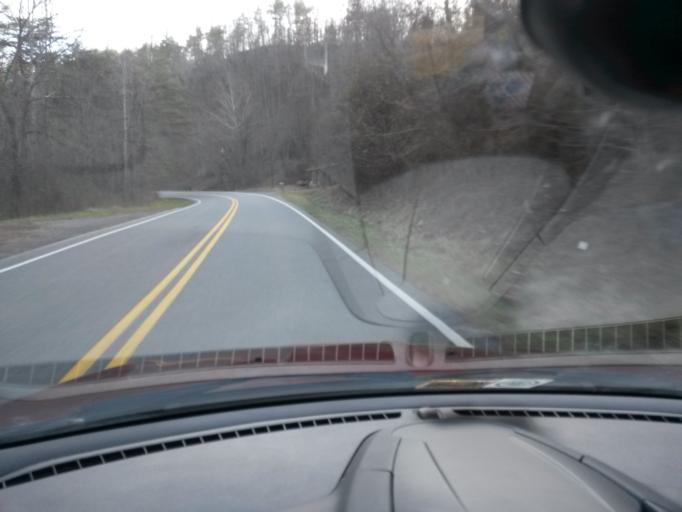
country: US
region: Virginia
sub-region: Alleghany County
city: Clifton Forge
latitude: 37.8578
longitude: -79.7466
